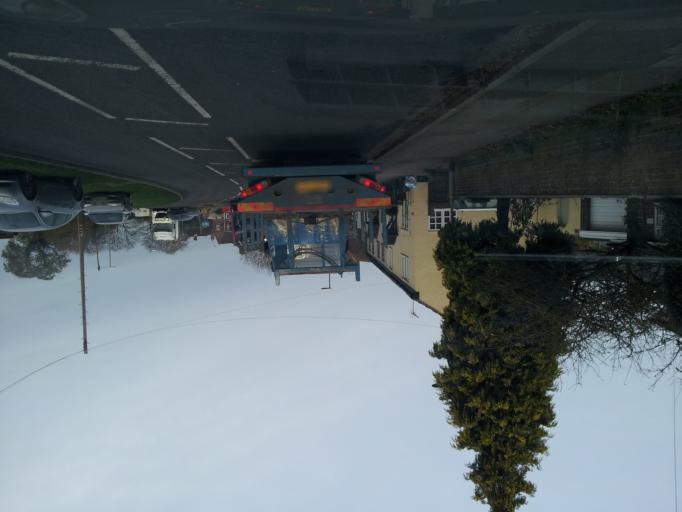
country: GB
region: England
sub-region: Buckinghamshire
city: Stewkley
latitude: 51.8973
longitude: -0.7145
